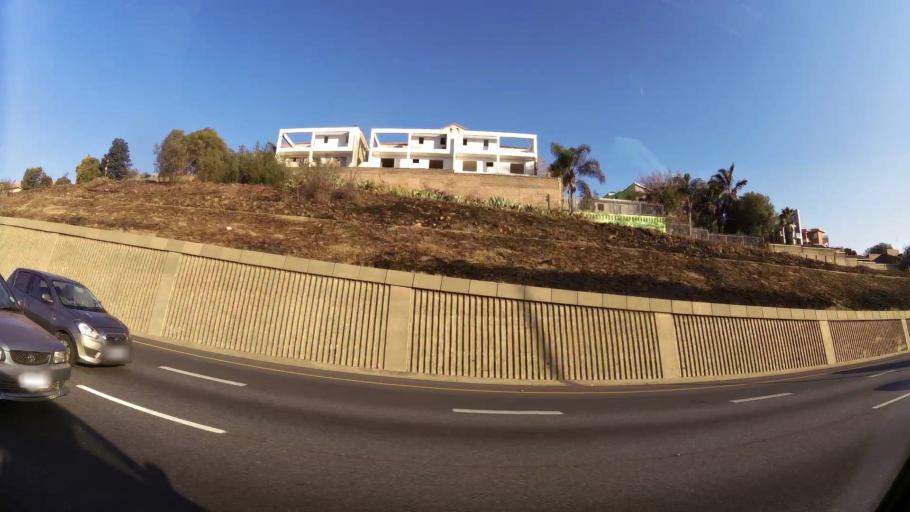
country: ZA
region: Gauteng
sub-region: City of Johannesburg Metropolitan Municipality
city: Johannesburg
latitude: -26.2692
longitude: 28.0587
